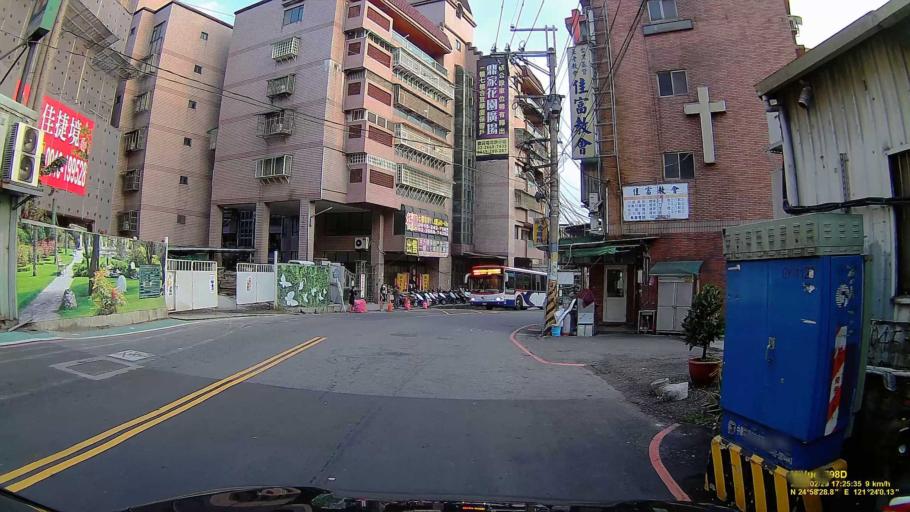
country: TW
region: Taipei
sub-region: Taipei
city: Banqiao
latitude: 24.9746
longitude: 121.4001
